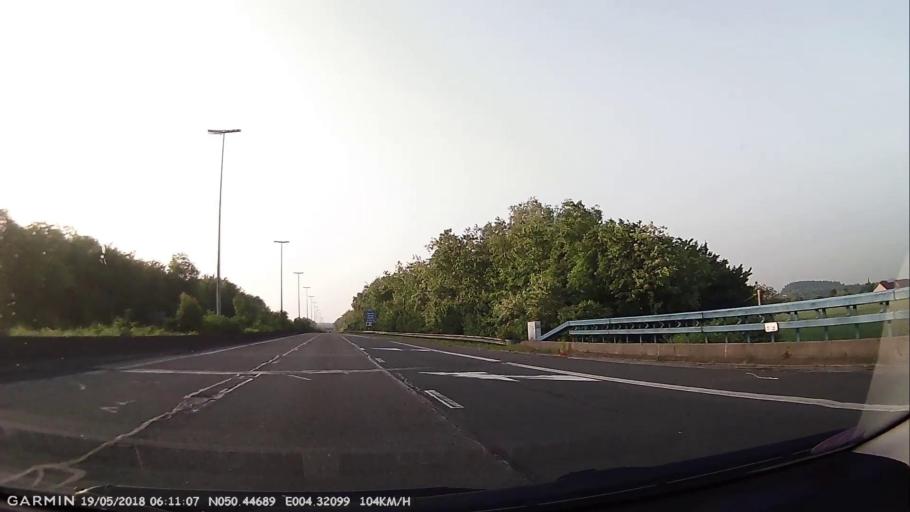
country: BE
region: Wallonia
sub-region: Province du Hainaut
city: Chapelle-lez-Herlaimont
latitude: 50.4467
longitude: 4.3213
